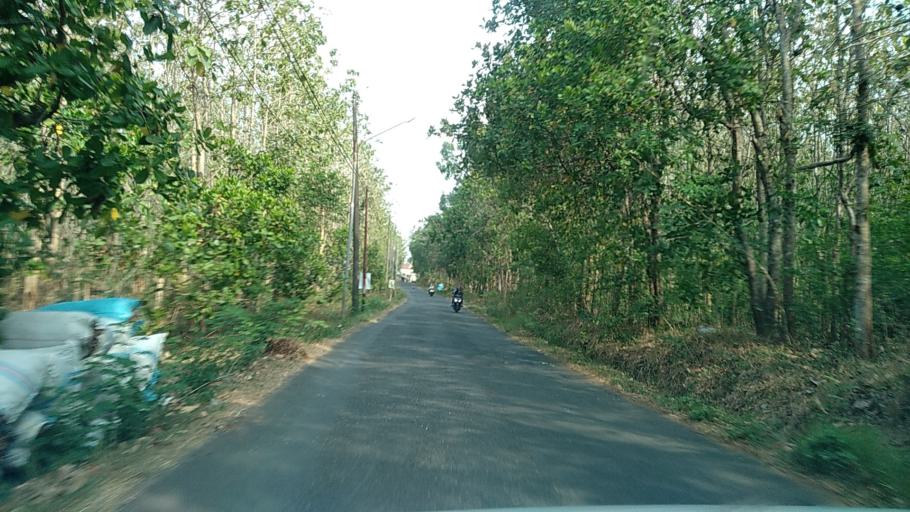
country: ID
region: Central Java
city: Semarang
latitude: -7.0445
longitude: 110.3097
